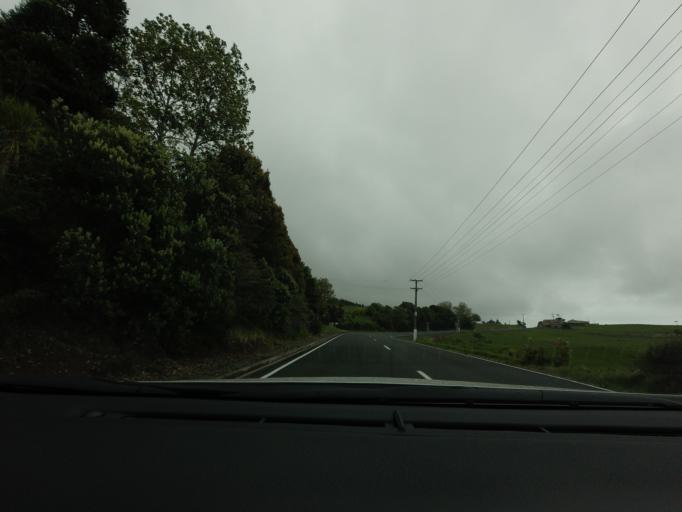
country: NZ
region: Auckland
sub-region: Auckland
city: Warkworth
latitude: -36.2887
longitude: 174.7978
